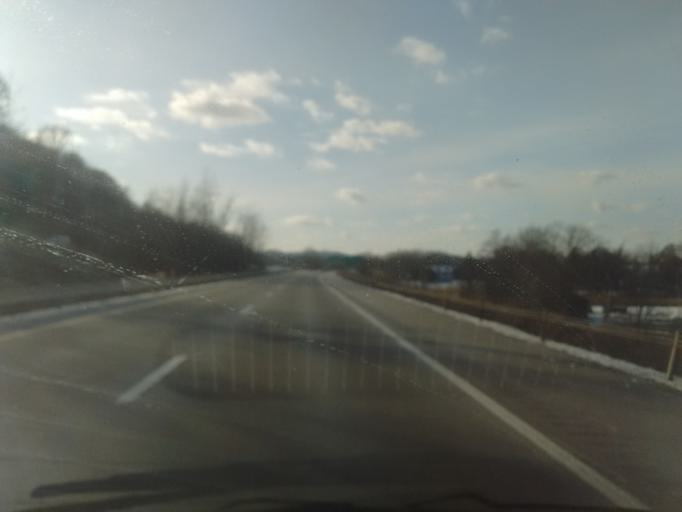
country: US
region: New York
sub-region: Dutchess County
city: Hillside Lake
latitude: 41.5409
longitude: -73.7618
